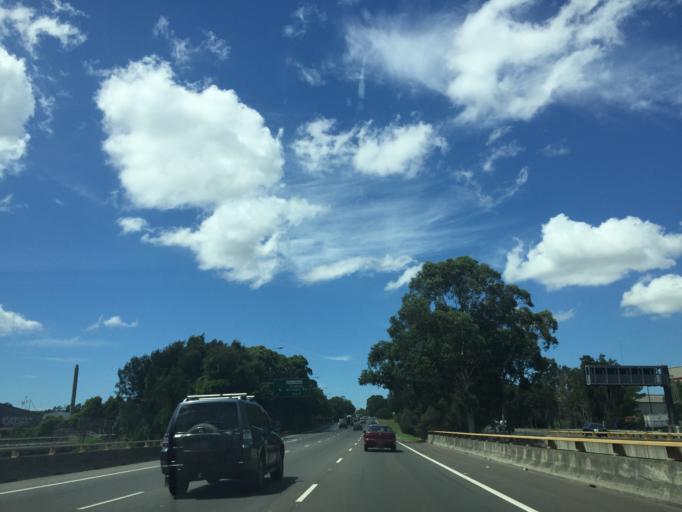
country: AU
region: New South Wales
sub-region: Auburn
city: Auburn
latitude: -33.8469
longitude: 151.0502
